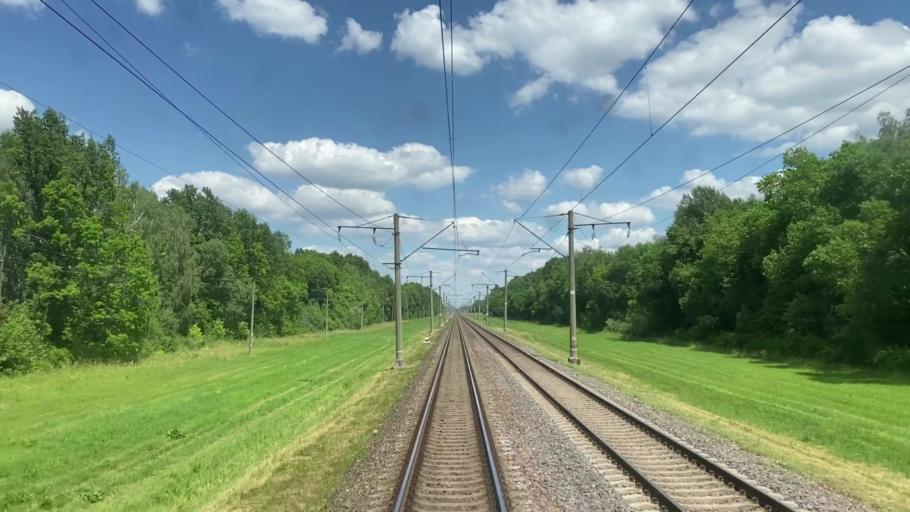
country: BY
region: Brest
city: Zhabinka
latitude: 52.2461
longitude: 24.1092
